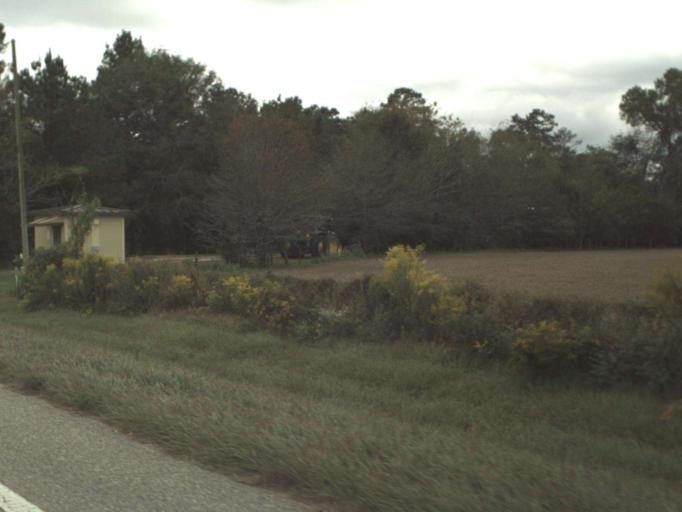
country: US
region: Florida
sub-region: Calhoun County
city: Blountstown
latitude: 30.5694
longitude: -85.0218
